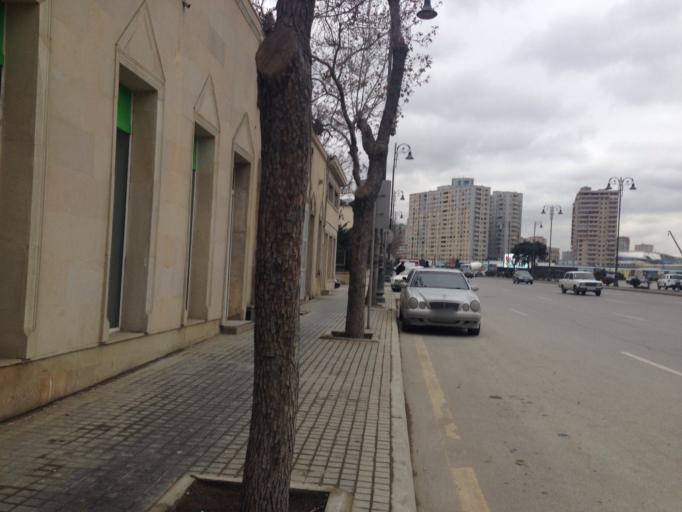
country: AZ
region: Baki
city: Baku
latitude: 40.3862
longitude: 49.8631
